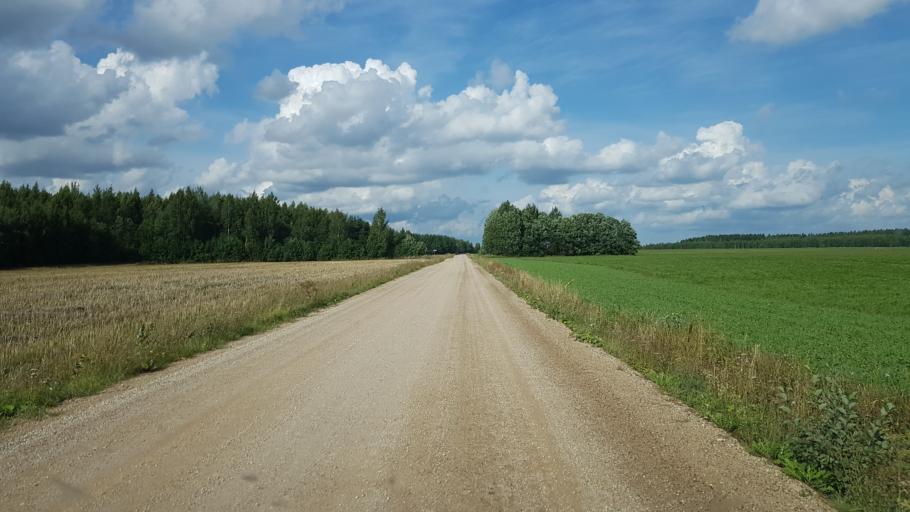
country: RU
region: Pskov
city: Pechory
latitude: 57.7796
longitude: 27.4707
